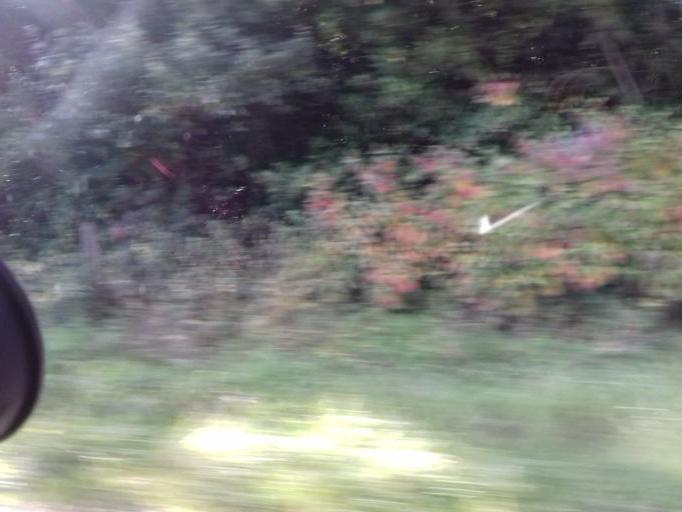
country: IE
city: Kentstown
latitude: 53.6384
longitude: -6.4966
